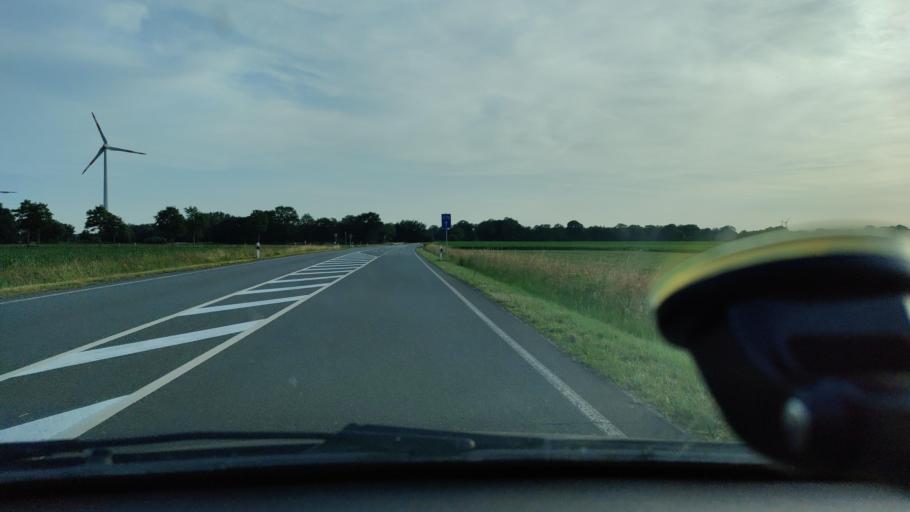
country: DE
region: North Rhine-Westphalia
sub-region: Regierungsbezirk Munster
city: Legden
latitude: 51.9777
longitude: 7.0949
